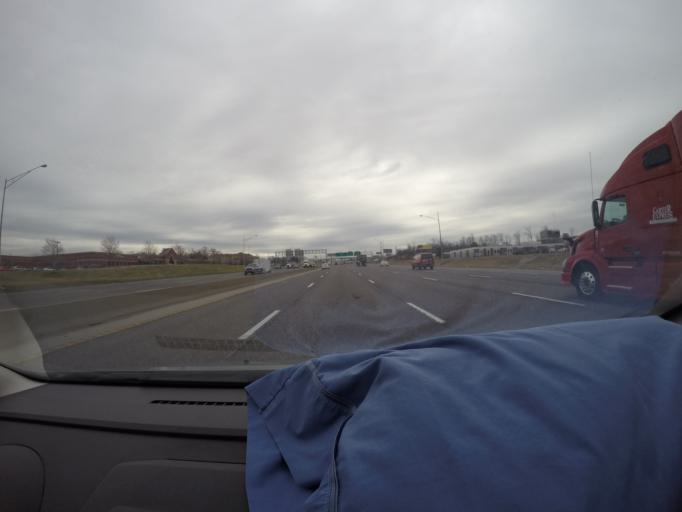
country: US
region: Missouri
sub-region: Saint Charles County
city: Saint Charles
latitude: 38.7538
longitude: -90.4537
